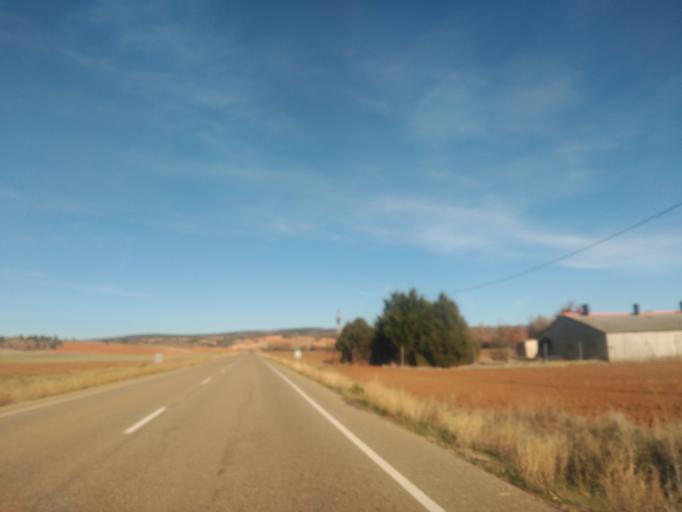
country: ES
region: Castille and Leon
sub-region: Provincia de Burgos
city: Huerta del Rey
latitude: 41.7965
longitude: -3.3436
